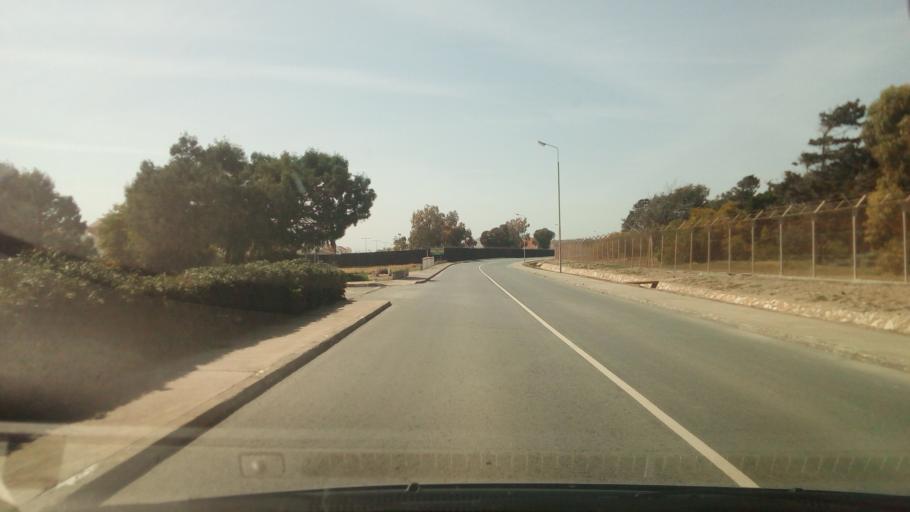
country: CY
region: Larnaka
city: Xylotymbou
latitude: 34.9819
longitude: 33.7264
